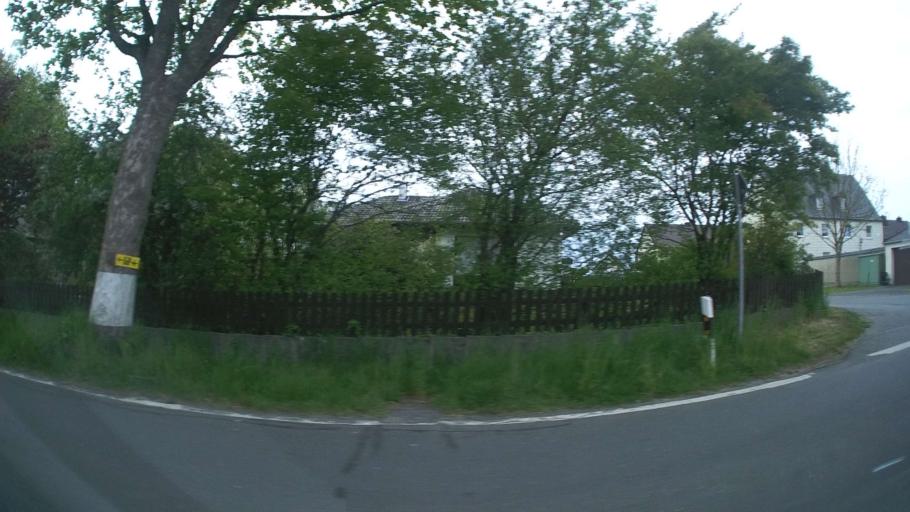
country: DE
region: Bavaria
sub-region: Upper Franconia
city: Sparneck
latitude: 50.1628
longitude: 11.8357
